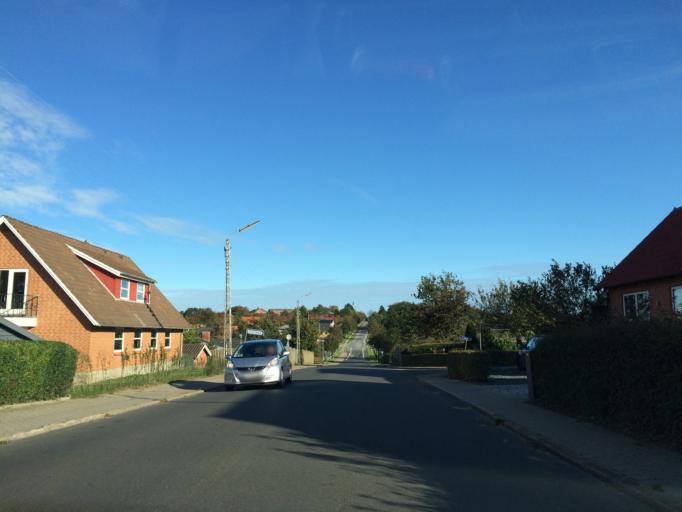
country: DK
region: Central Jutland
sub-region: Favrskov Kommune
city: Hammel
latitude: 56.3004
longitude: 9.7860
